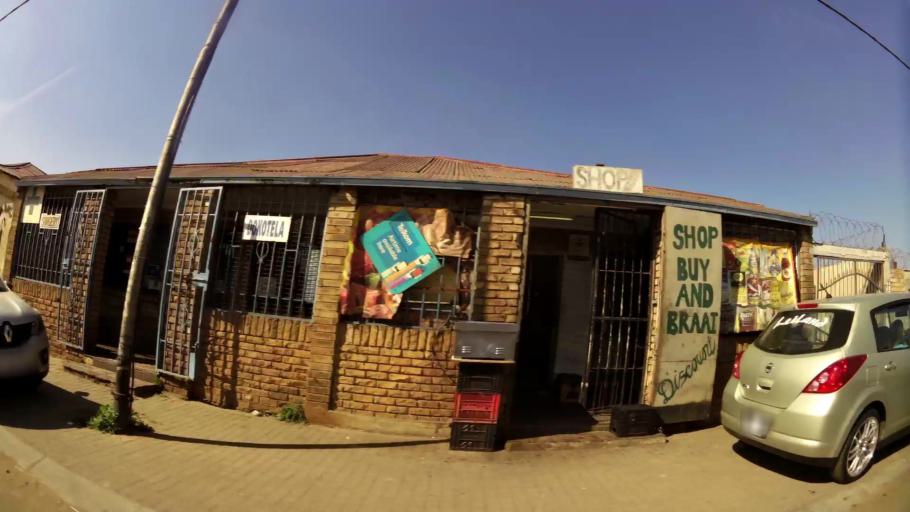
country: ZA
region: Gauteng
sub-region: City of Johannesburg Metropolitan Municipality
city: Johannesburg
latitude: -26.1829
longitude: 27.9655
